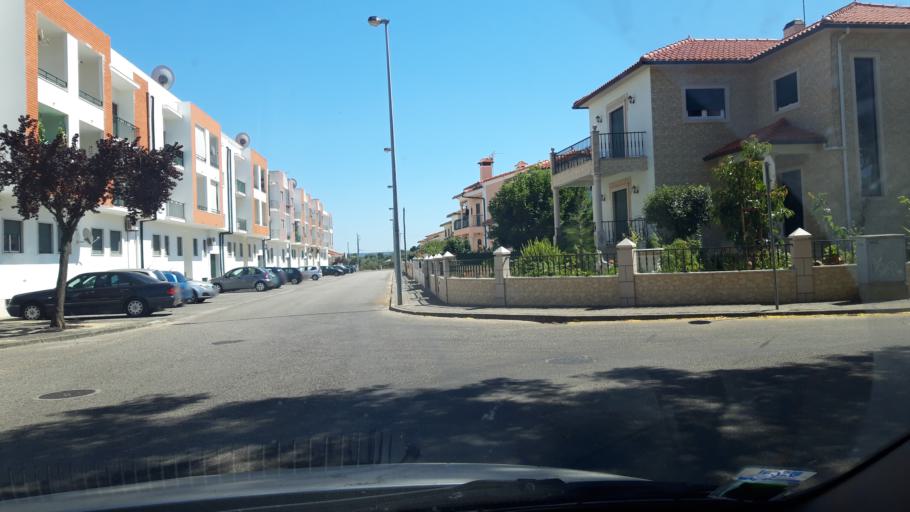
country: PT
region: Santarem
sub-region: Entroncamento
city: Entroncamento
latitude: 39.4644
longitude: -8.4527
